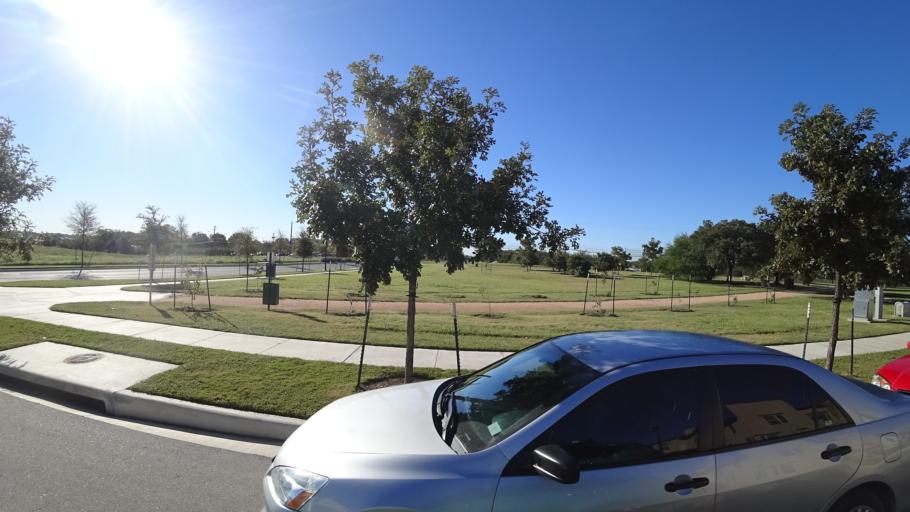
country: US
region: Texas
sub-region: Travis County
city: Austin
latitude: 30.2909
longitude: -97.6953
